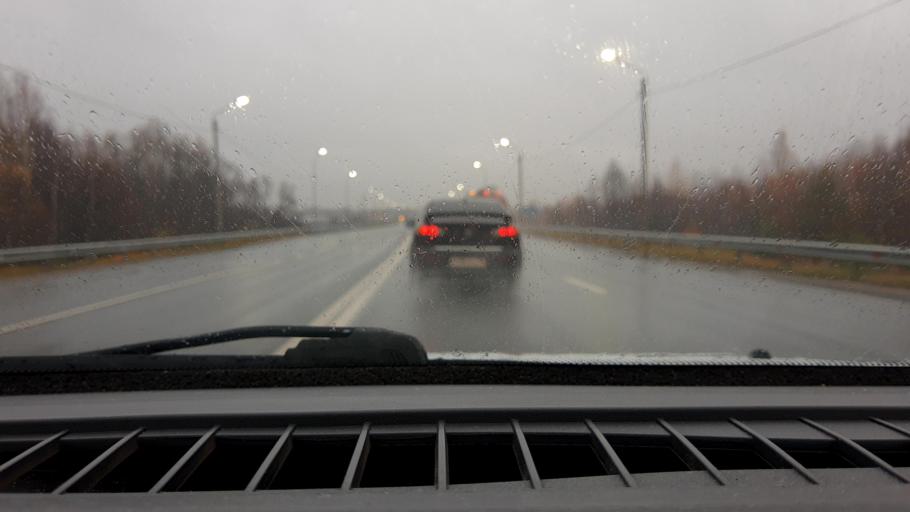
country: RU
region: Nizjnij Novgorod
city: Sitniki
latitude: 56.5060
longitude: 44.0235
